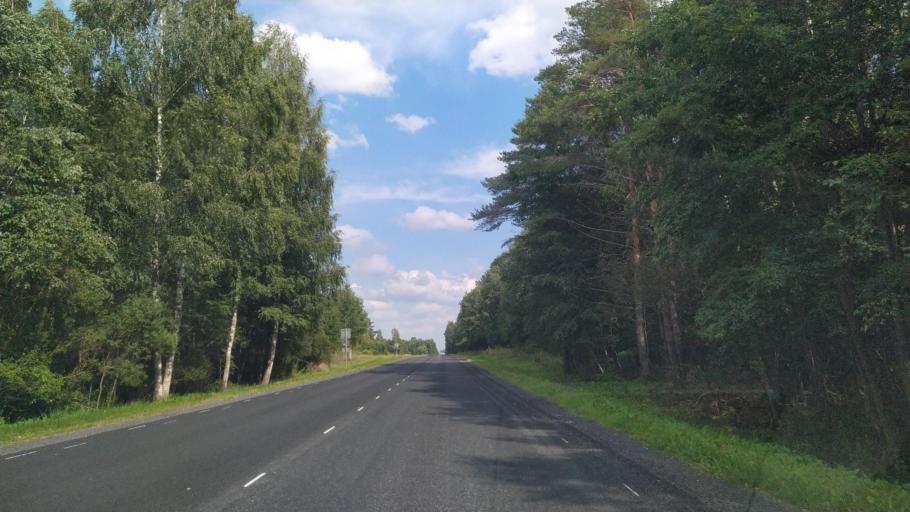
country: RU
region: Pskov
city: Porkhov
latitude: 57.7406
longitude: 29.4243
